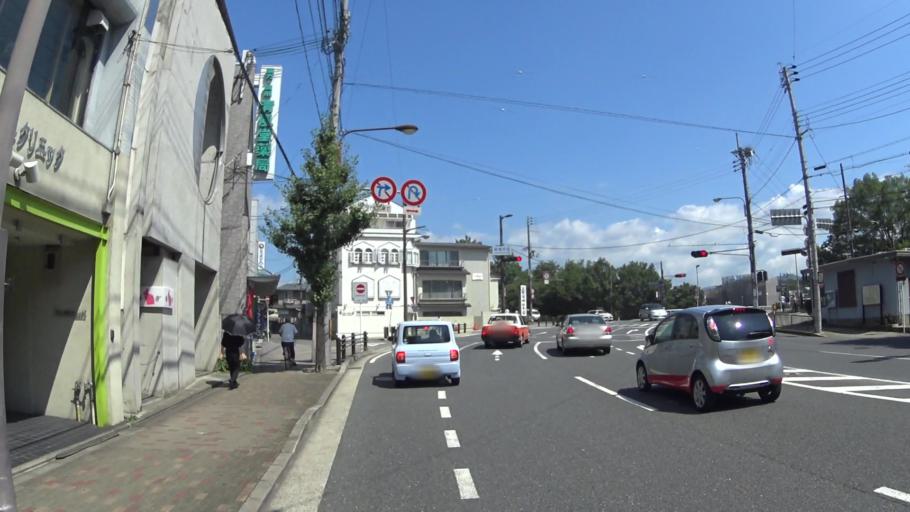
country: JP
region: Kyoto
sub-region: Kyoto-shi
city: Kamigyo-ku
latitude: 35.0316
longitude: 135.7696
